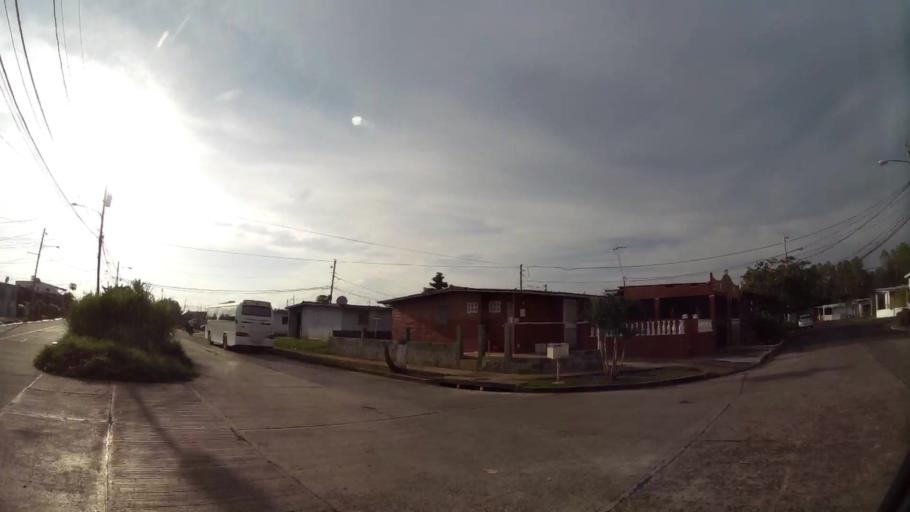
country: PA
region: Panama
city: Cabra Numero Uno
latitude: 9.0814
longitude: -79.3526
